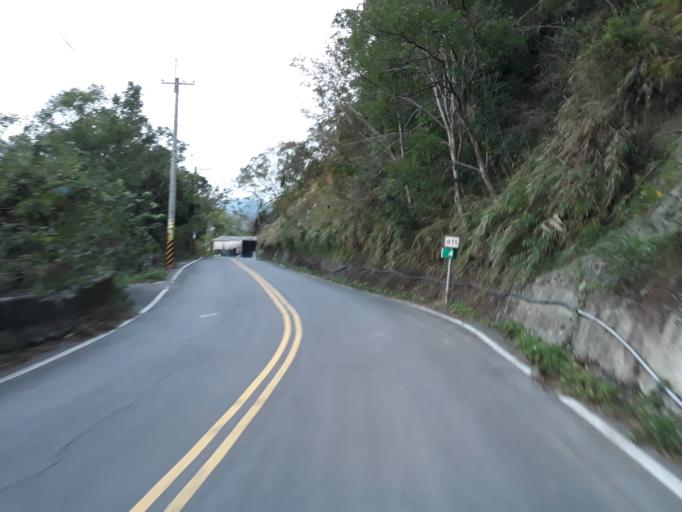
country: TW
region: Taiwan
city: Fengyuan
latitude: 24.3682
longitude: 120.8668
